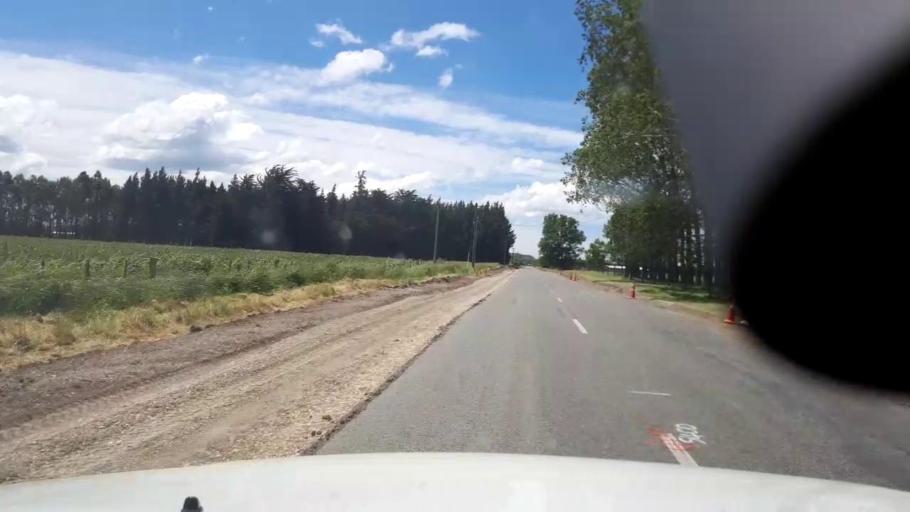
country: NZ
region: Canterbury
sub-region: Timaru District
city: Pleasant Point
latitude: -44.2774
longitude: 171.2495
